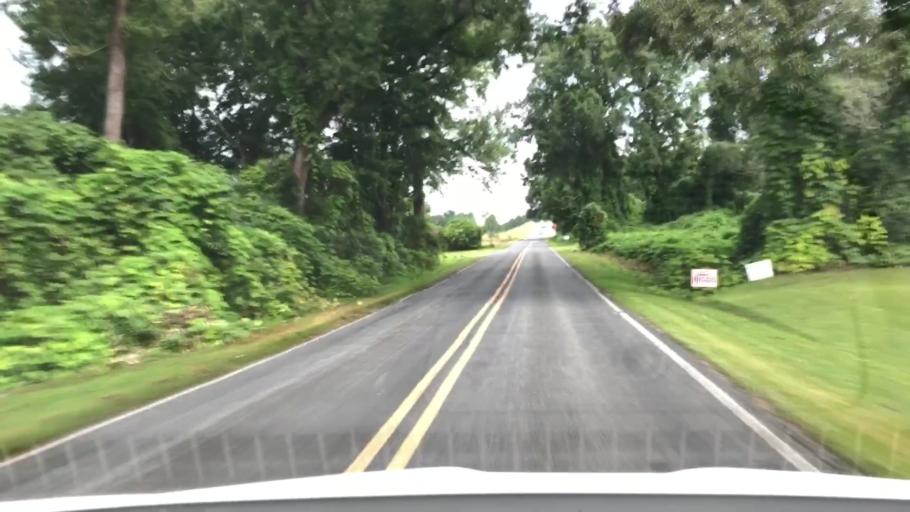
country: US
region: North Carolina
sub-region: Jones County
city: Maysville
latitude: 34.9079
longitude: -77.2341
